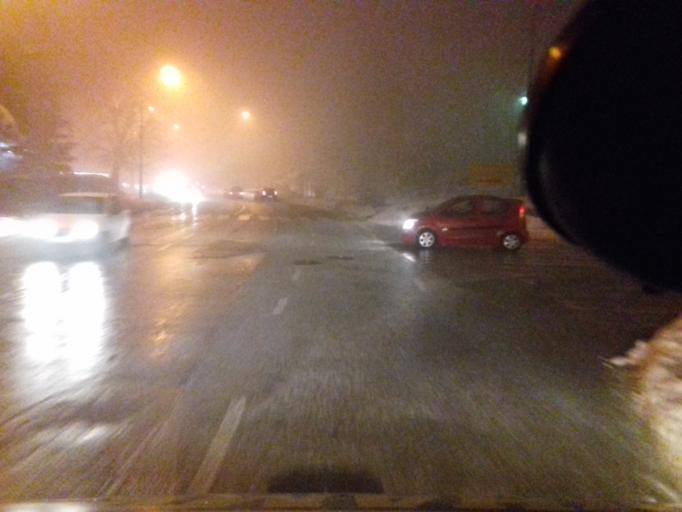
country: BA
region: Federation of Bosnia and Herzegovina
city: Kobilja Glava
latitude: 43.8671
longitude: 18.4165
